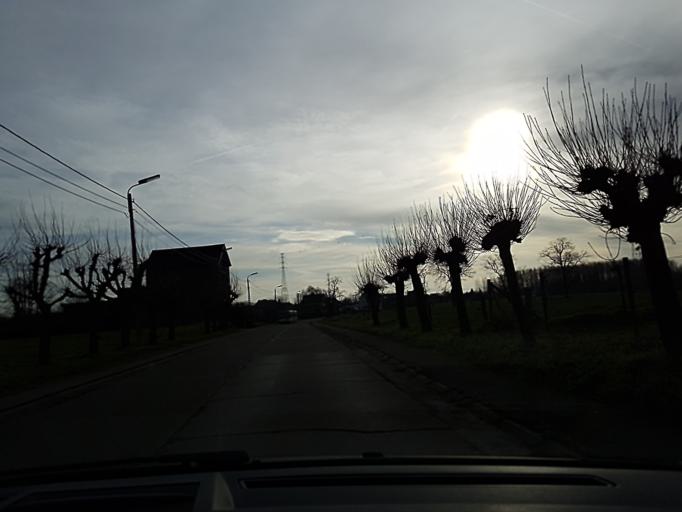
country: BE
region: Flanders
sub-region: Provincie Vlaams-Brabant
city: Rotselaar
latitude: 50.9460
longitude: 4.6811
